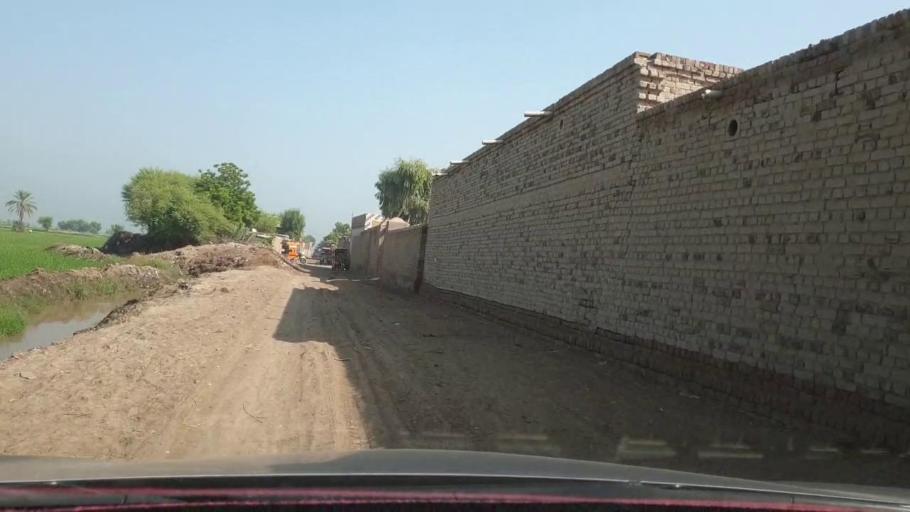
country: PK
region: Sindh
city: Kambar
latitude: 27.6022
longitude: 67.9360
